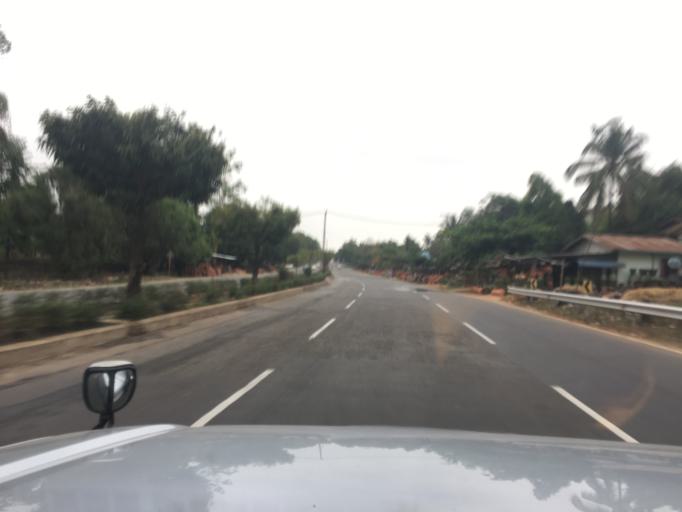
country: MM
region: Bago
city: Bago
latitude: 17.2346
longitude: 96.4615
